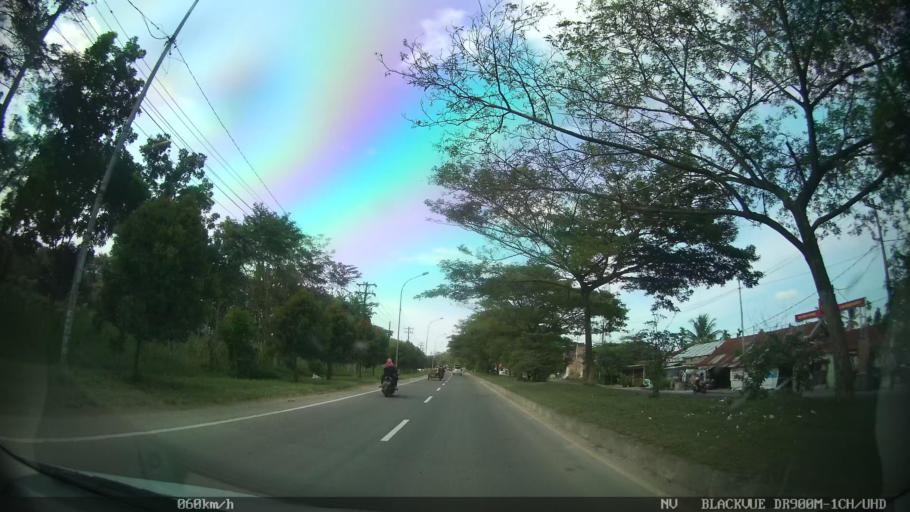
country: ID
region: North Sumatra
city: Percut
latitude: 3.5739
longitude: 98.7994
